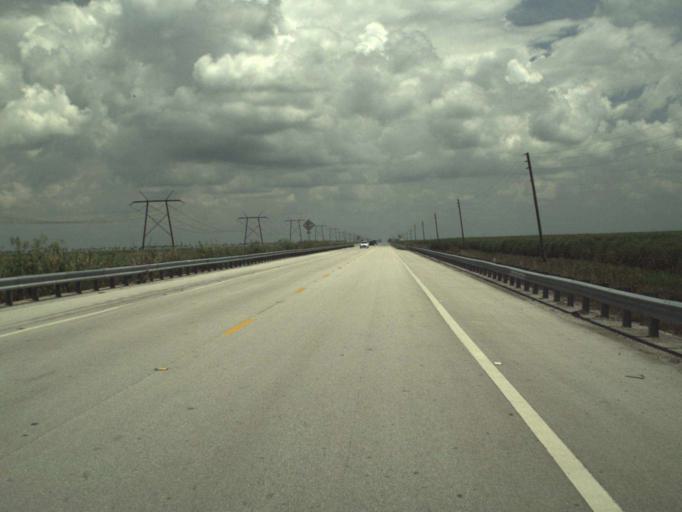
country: US
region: Florida
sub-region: Palm Beach County
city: Pahokee
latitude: 26.8272
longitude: -80.5824
